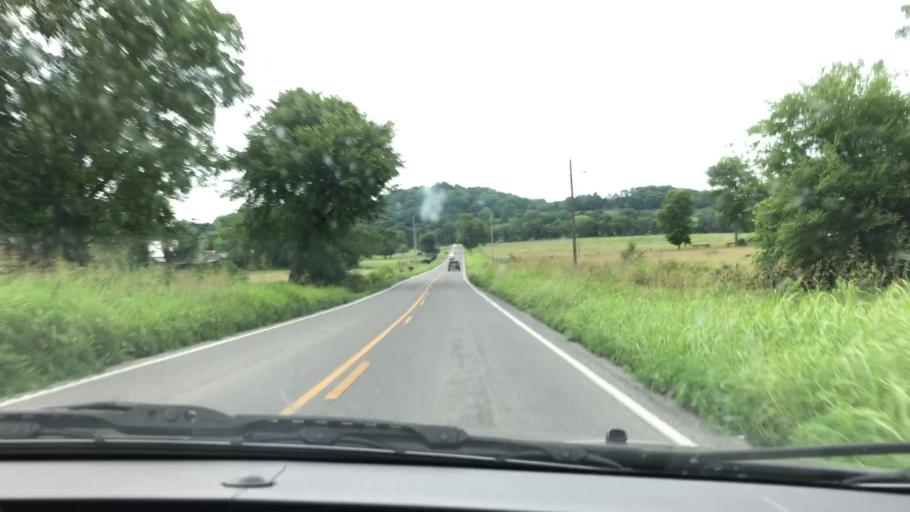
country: US
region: Tennessee
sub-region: Maury County
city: Spring Hill
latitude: 35.7876
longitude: -87.0039
